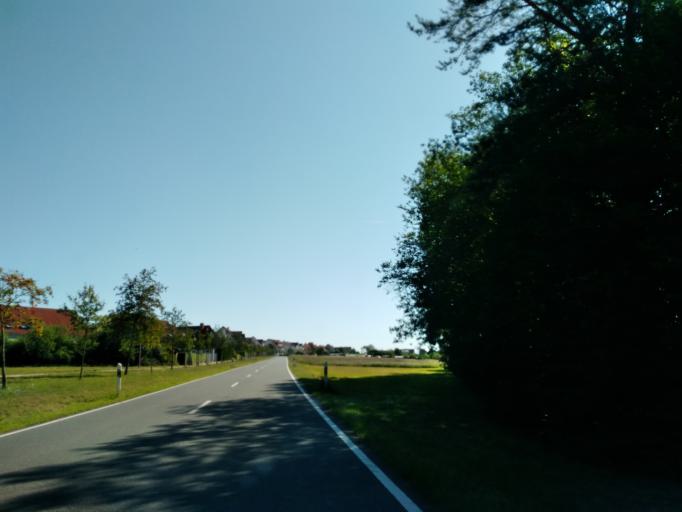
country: DE
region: Baden-Wuerttemberg
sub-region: Karlsruhe Region
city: Buchen
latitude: 49.5159
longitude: 9.2986
